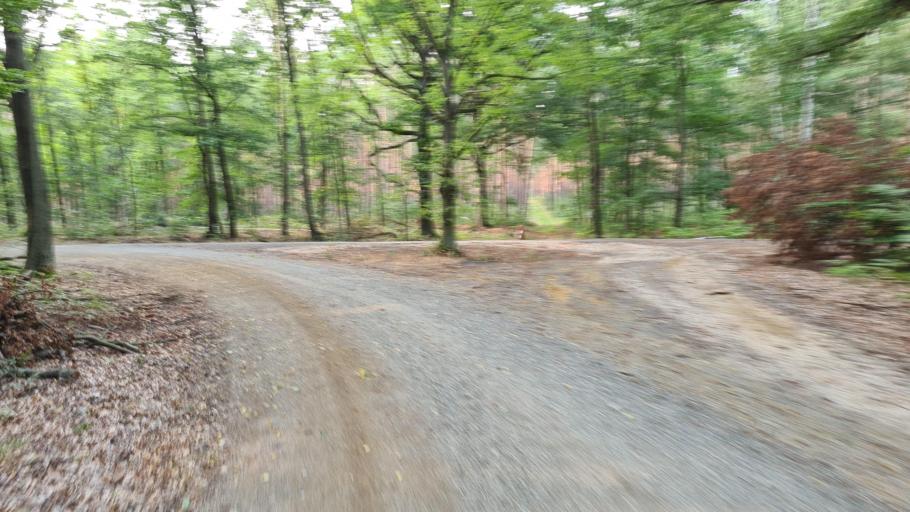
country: DE
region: Brandenburg
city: Trobitz
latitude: 51.6338
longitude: 13.4522
